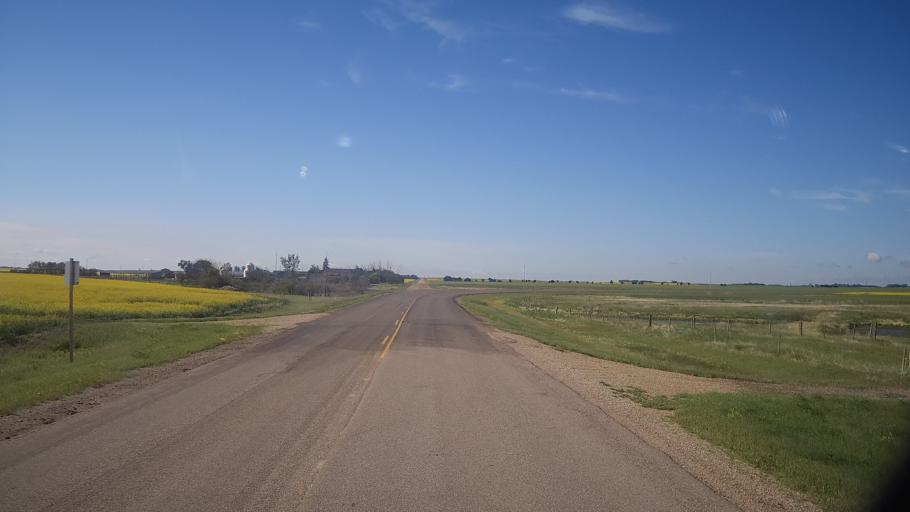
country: CA
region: Saskatchewan
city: Watrous
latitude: 51.6823
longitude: -105.3809
